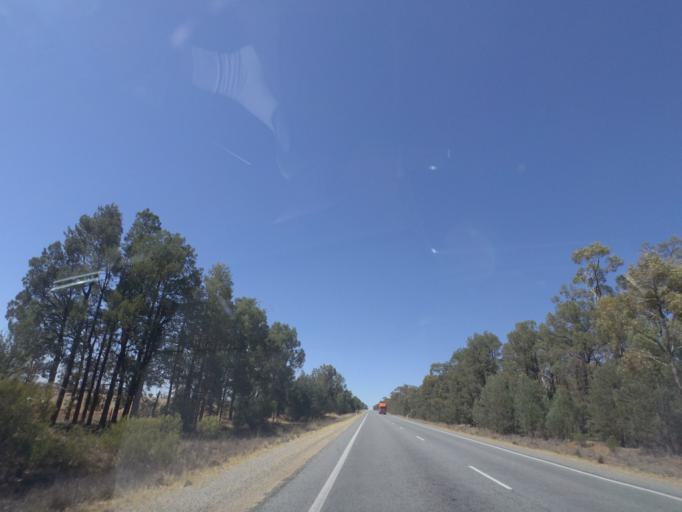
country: AU
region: New South Wales
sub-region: Narrandera
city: Narrandera
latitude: -34.4280
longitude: 146.8437
